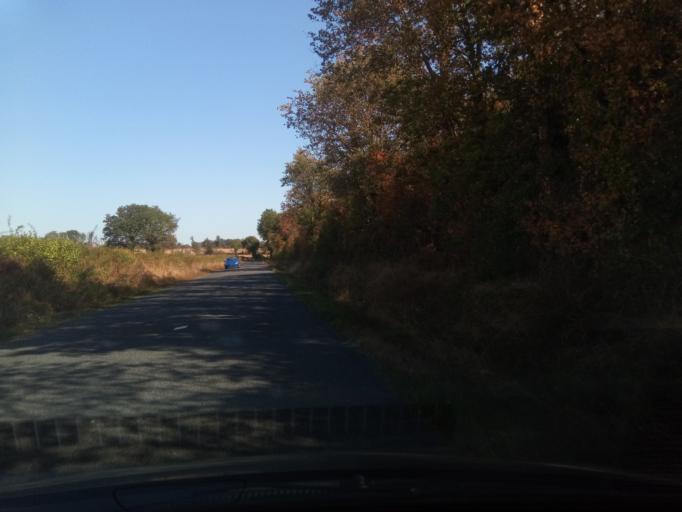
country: FR
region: Poitou-Charentes
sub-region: Departement de la Vienne
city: Saulge
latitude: 46.3505
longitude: 0.8714
